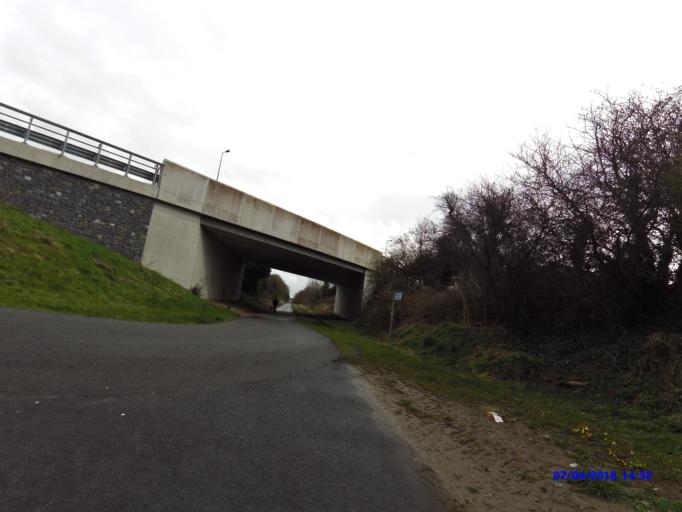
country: IE
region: Leinster
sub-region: An Iarmhi
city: Athlone
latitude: 53.4226
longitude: -7.9006
